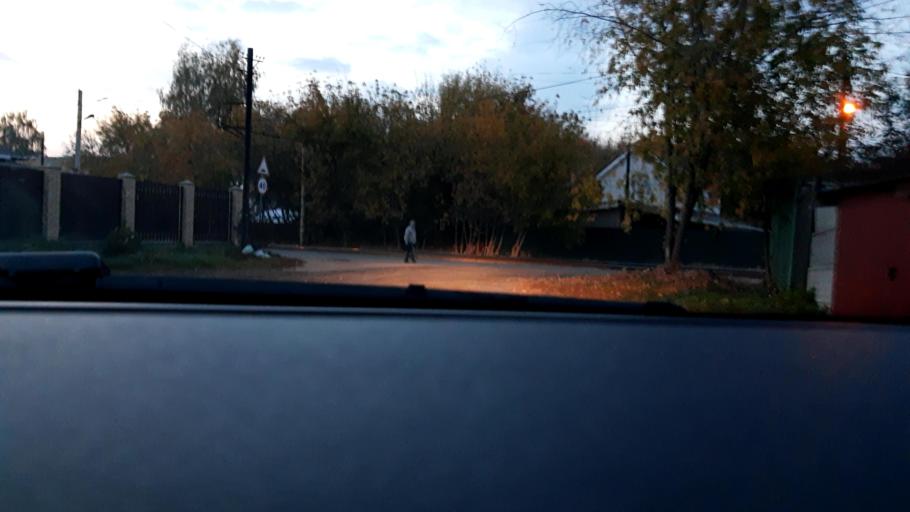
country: RU
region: Nizjnij Novgorod
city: Nizhniy Novgorod
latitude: 56.3345
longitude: 43.9129
